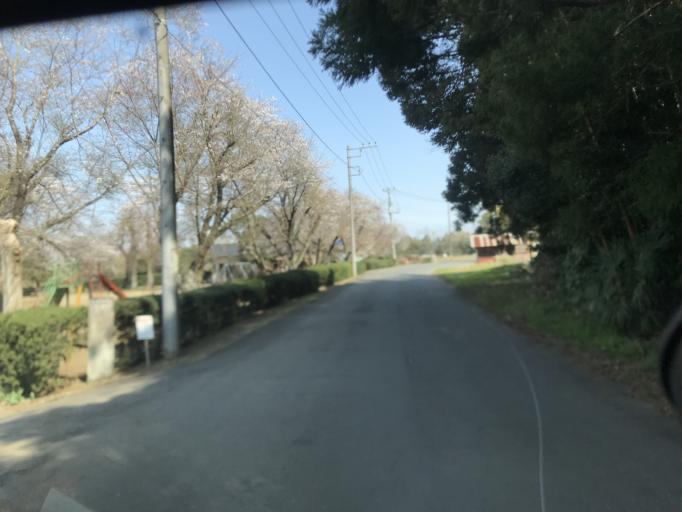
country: JP
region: Chiba
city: Sawara
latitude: 35.8490
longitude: 140.5245
